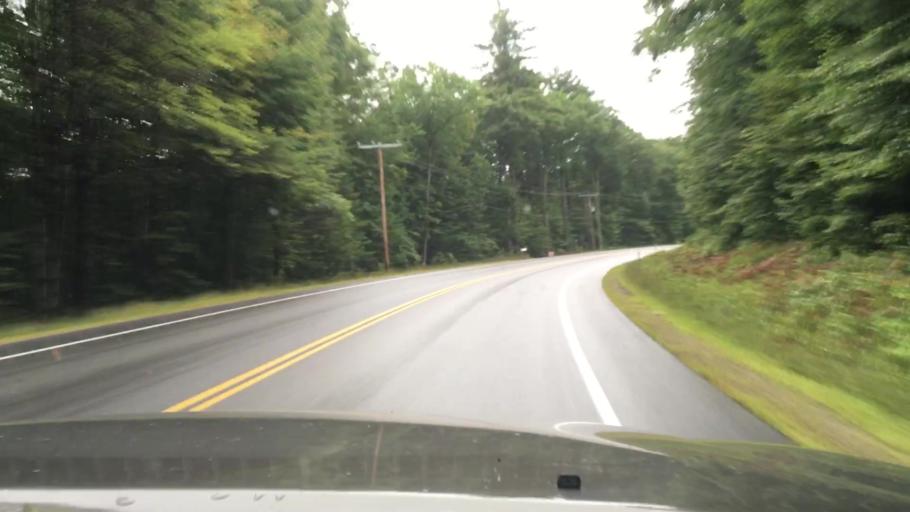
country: US
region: New Hampshire
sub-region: Hillsborough County
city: Antrim
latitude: 43.0856
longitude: -71.9652
